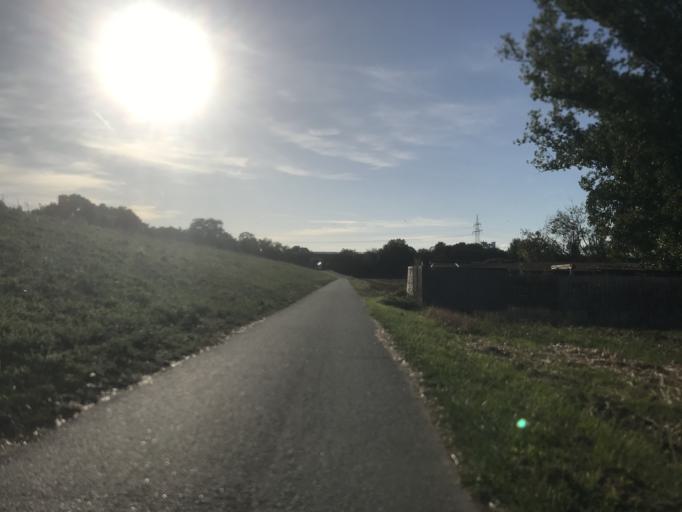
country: DE
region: Hesse
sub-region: Regierungsbezirk Darmstadt
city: Hochheim am Main
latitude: 49.9970
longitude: 8.3493
